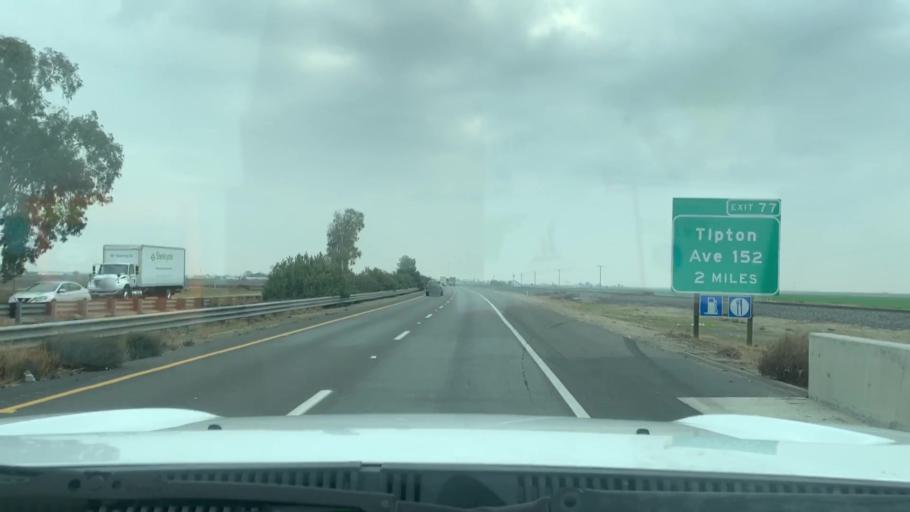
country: US
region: California
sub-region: Tulare County
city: Tipton
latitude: 36.0935
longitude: -119.3223
